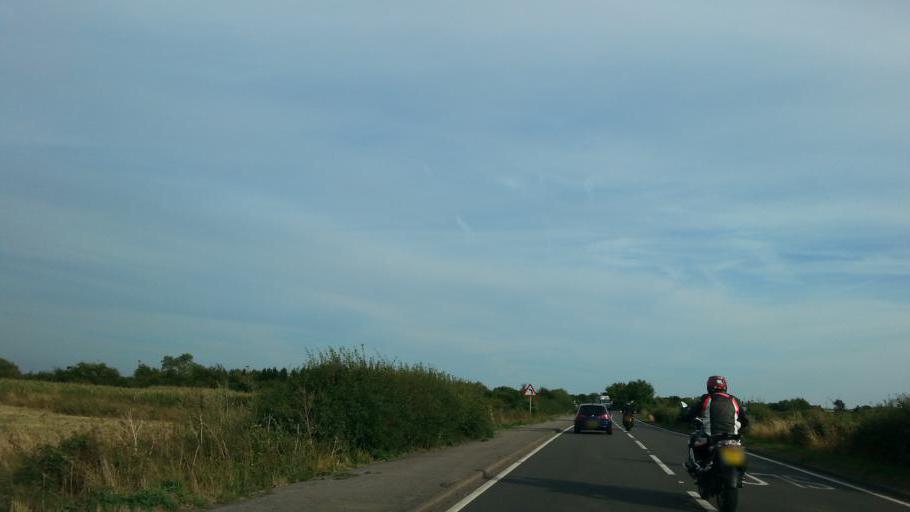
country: GB
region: England
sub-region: Nottinghamshire
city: Newark on Trent
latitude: 53.0857
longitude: -0.8340
